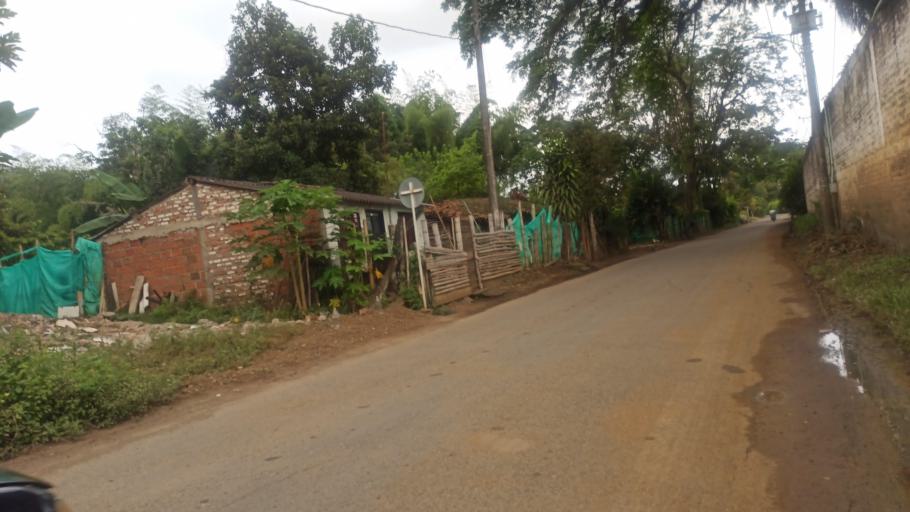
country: CO
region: Valle del Cauca
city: Jamundi
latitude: 3.2006
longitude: -76.5096
